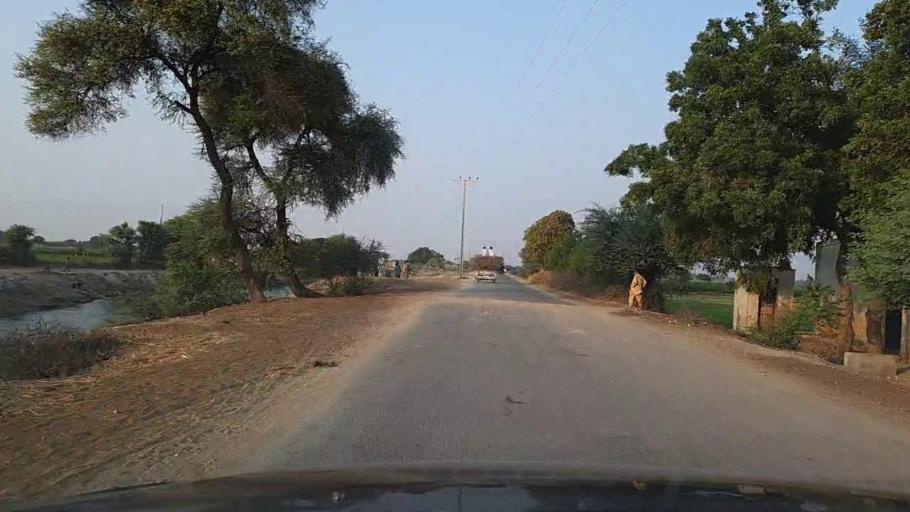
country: PK
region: Sindh
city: Mirpur Sakro
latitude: 24.5342
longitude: 67.8308
